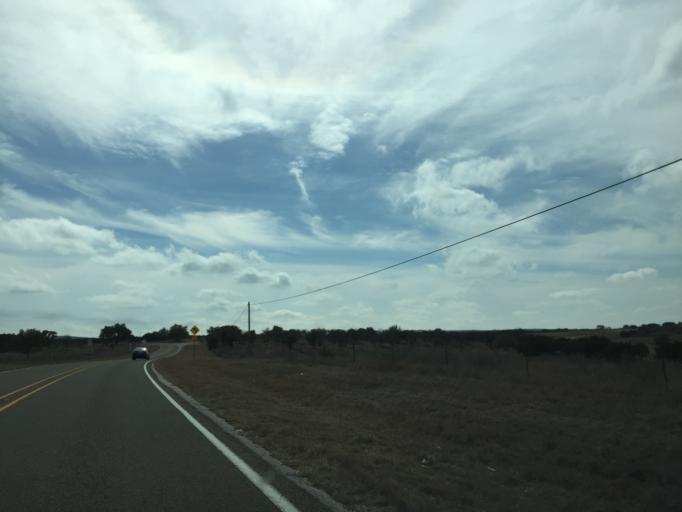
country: US
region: Texas
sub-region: Burnet County
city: Granite Shoals
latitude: 30.4943
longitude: -98.4381
